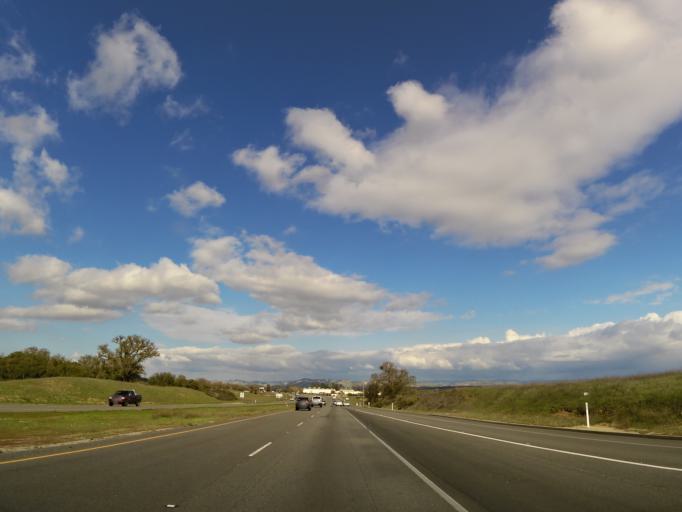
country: US
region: California
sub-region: San Luis Obispo County
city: Paso Robles
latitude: 35.6628
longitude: -120.6970
